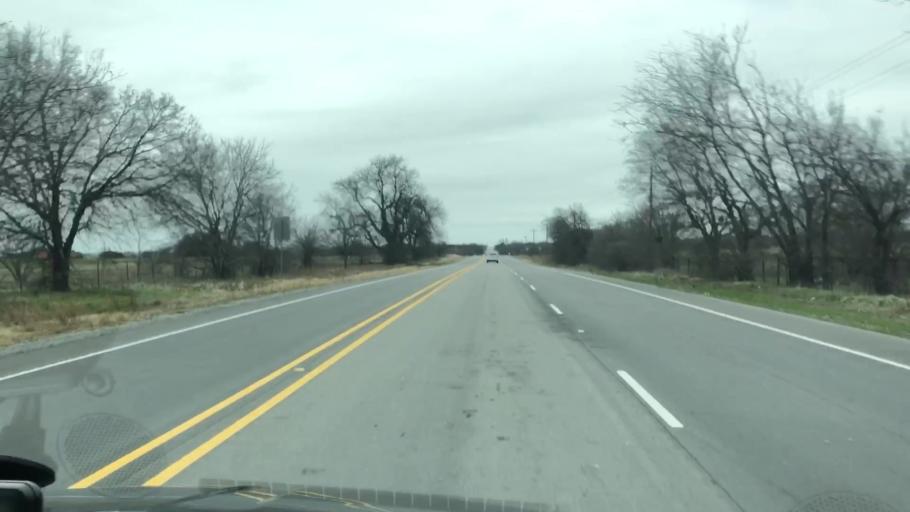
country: US
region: Texas
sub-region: Erath County
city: Stephenville
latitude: 32.1569
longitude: -98.1469
